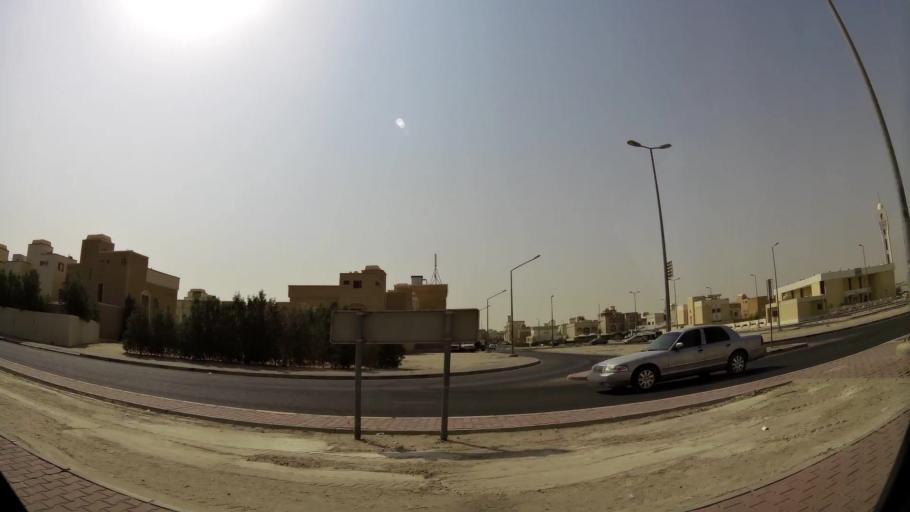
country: KW
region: Muhafazat al Jahra'
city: Al Jahra'
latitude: 29.3196
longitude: 47.7264
